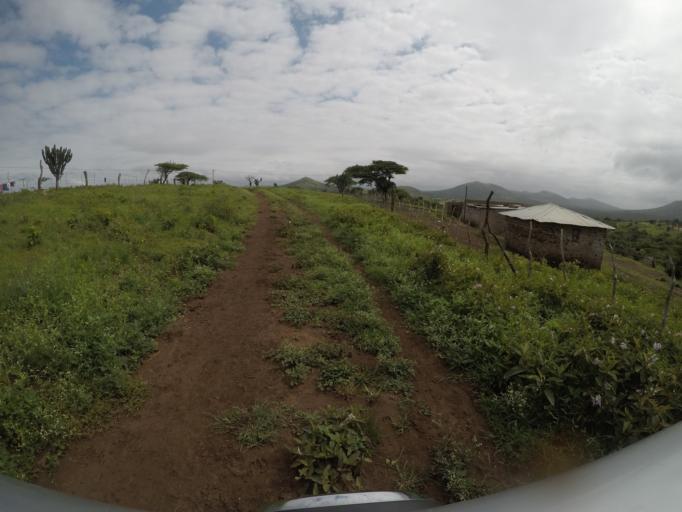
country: ZA
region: KwaZulu-Natal
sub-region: uThungulu District Municipality
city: Empangeni
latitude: -28.6274
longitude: 31.8638
